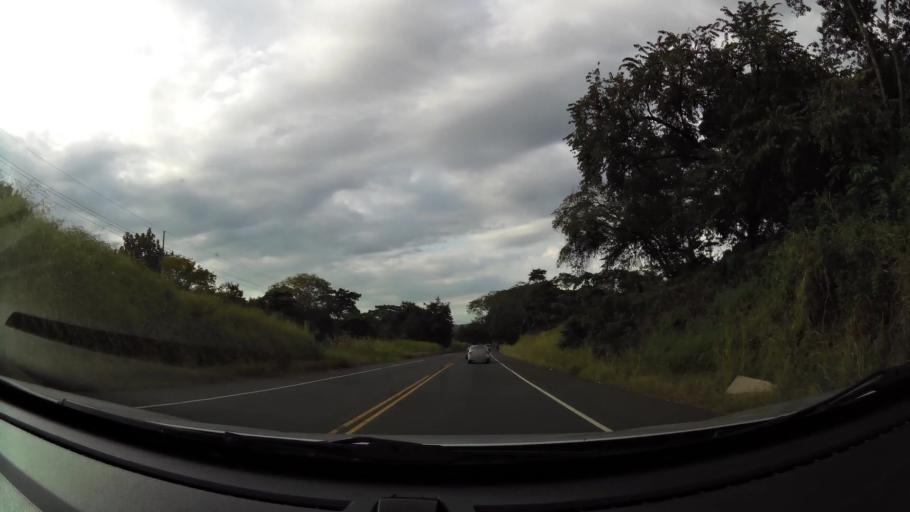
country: CR
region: Puntarenas
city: Esparza
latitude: 9.8990
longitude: -84.6575
